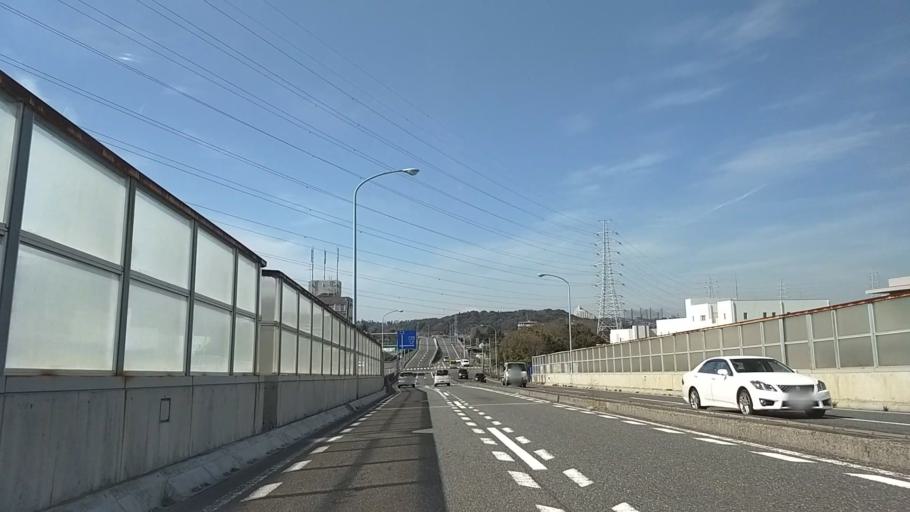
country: JP
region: Kanagawa
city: Kamakura
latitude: 35.3796
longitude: 139.5379
